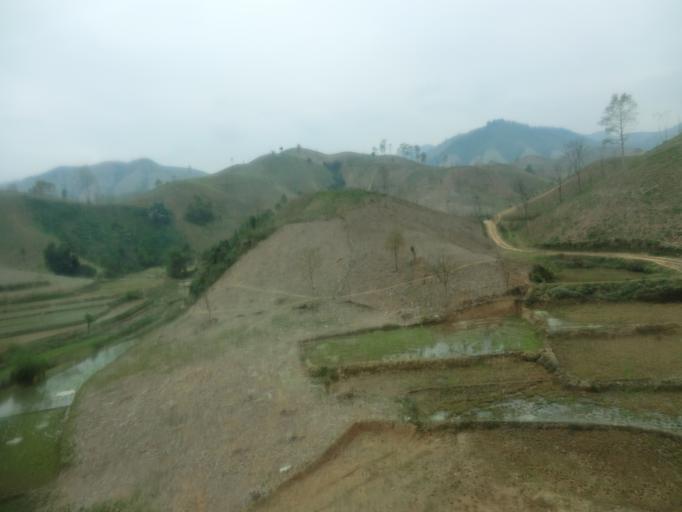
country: VN
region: Lao Cai
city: Thi Tran Pho Rang
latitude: 22.1358
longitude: 104.3861
